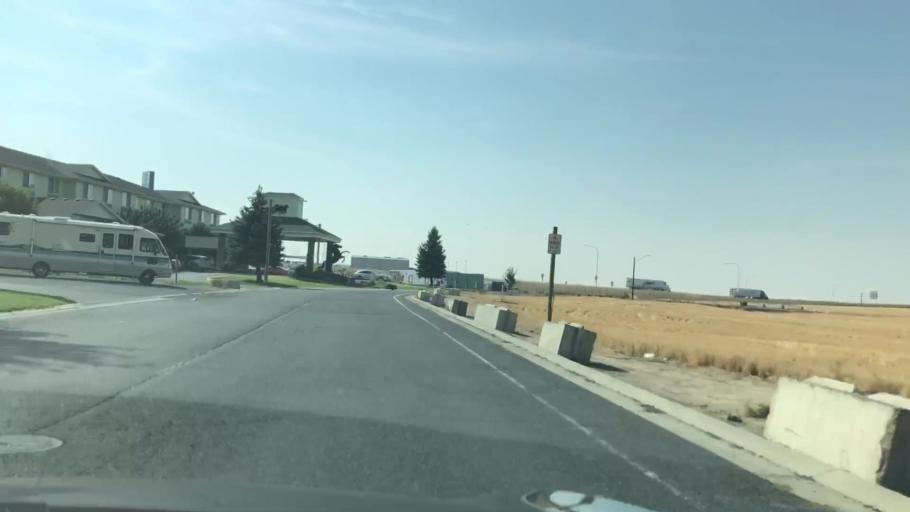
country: US
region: Washington
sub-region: Adams County
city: Ritzville
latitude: 47.1176
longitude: -118.3682
